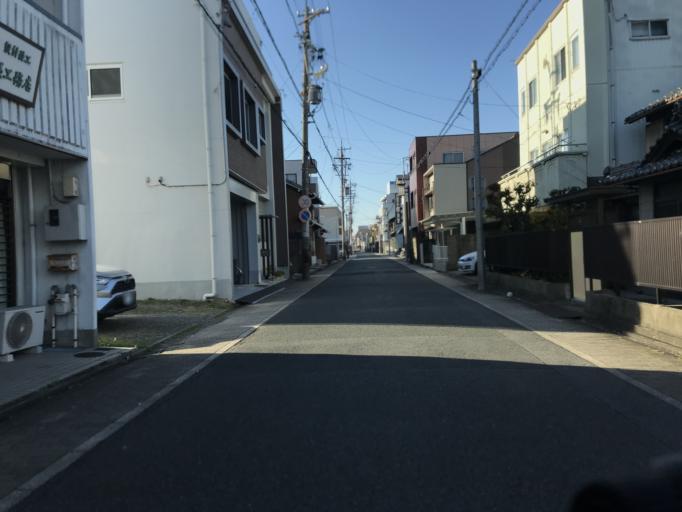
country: JP
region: Aichi
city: Nagoya-shi
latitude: 35.1899
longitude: 136.8757
